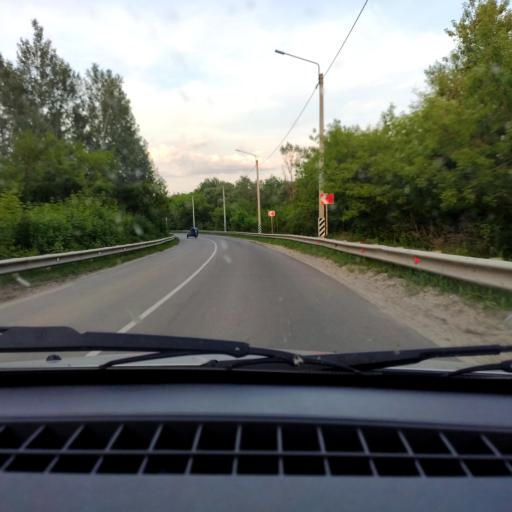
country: RU
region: Voronezj
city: Ramon'
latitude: 51.9490
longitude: 39.3752
